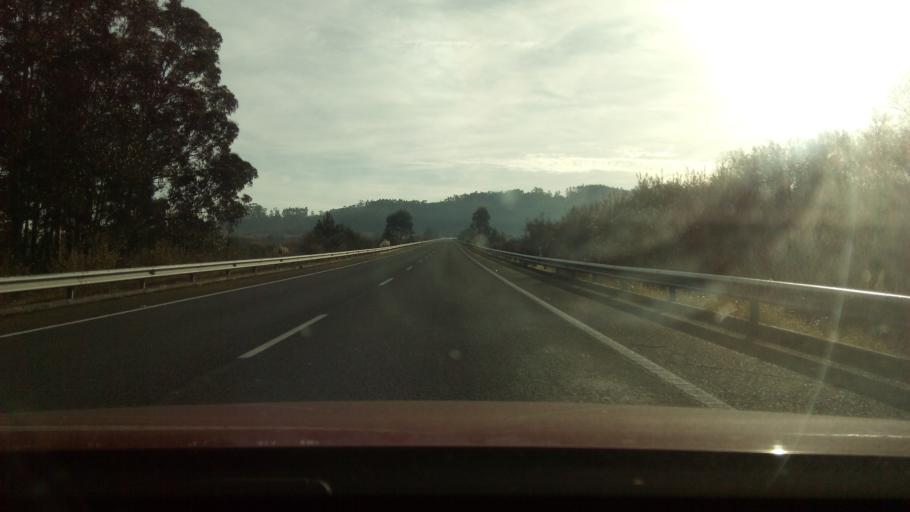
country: ES
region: Galicia
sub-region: Provincia de Pontevedra
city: O Grove
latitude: 42.4412
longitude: -8.8613
